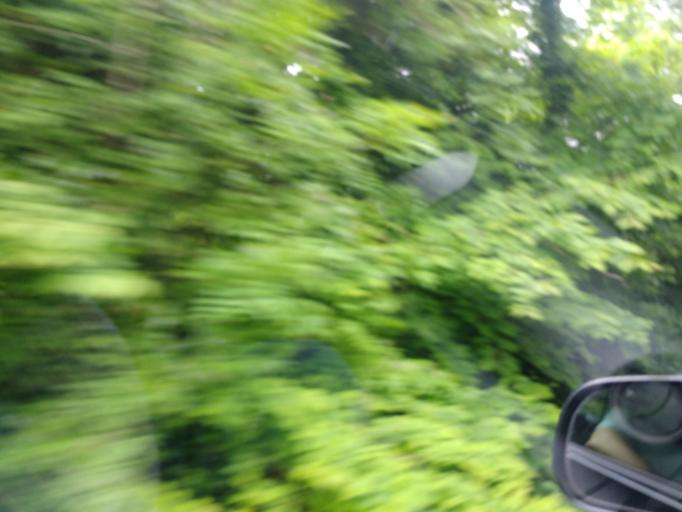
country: IE
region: Leinster
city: Portraine
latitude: 53.4813
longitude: -6.1190
